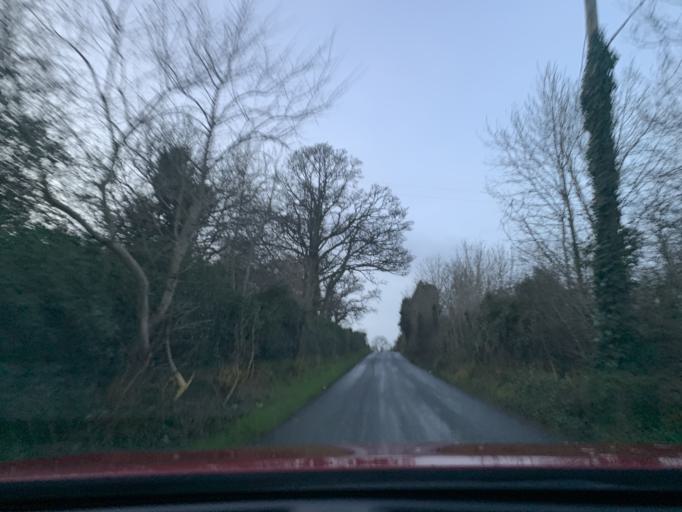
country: IE
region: Connaught
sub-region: Sligo
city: Ballymote
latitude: 54.1194
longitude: -8.5773
